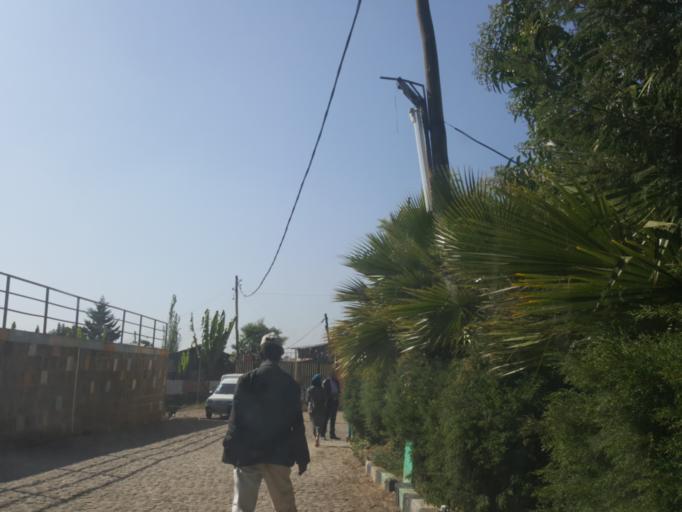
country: ET
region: Adis Abeba
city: Addis Ababa
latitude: 9.0507
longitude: 38.7327
